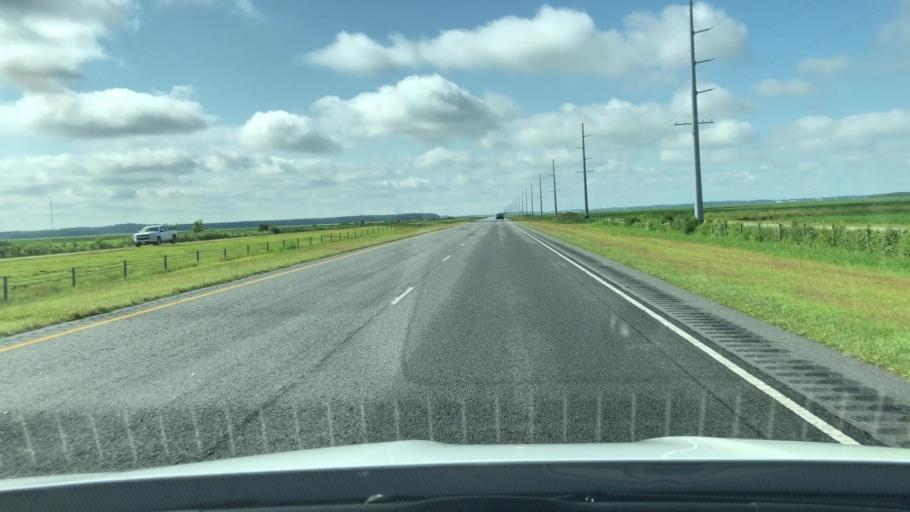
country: US
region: North Carolina
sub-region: Pasquotank County
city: Elizabeth City
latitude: 36.3286
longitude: -76.3112
